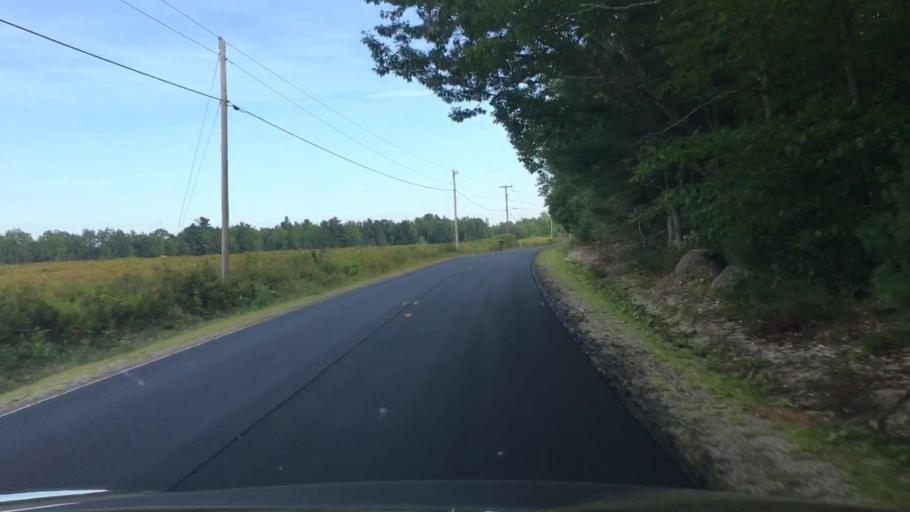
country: US
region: Maine
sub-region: Hancock County
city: Surry
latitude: 44.5364
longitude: -68.6146
